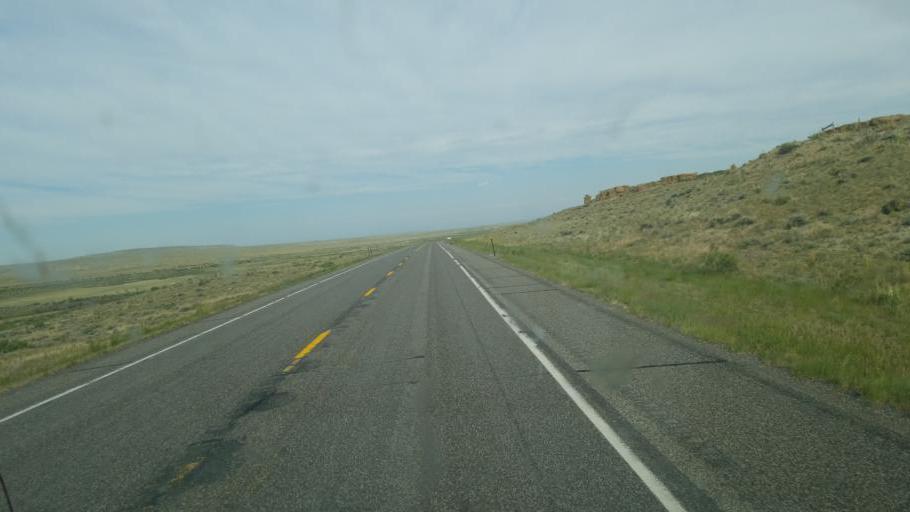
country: US
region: Wyoming
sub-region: Fremont County
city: Riverton
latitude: 43.2207
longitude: -108.0024
